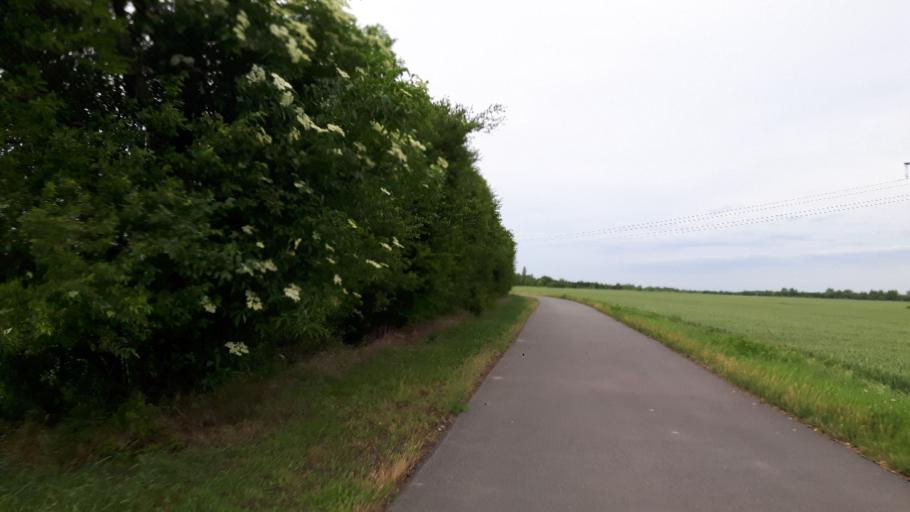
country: DE
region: Saxony
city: Rackwitz
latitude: 51.4179
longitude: 12.3193
